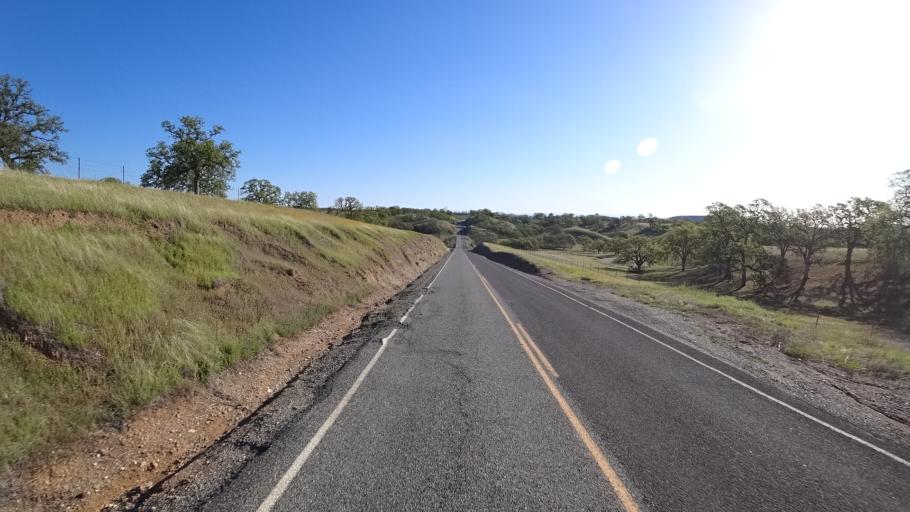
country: US
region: California
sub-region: Tehama County
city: Rancho Tehama Reserve
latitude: 39.8129
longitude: -122.3920
